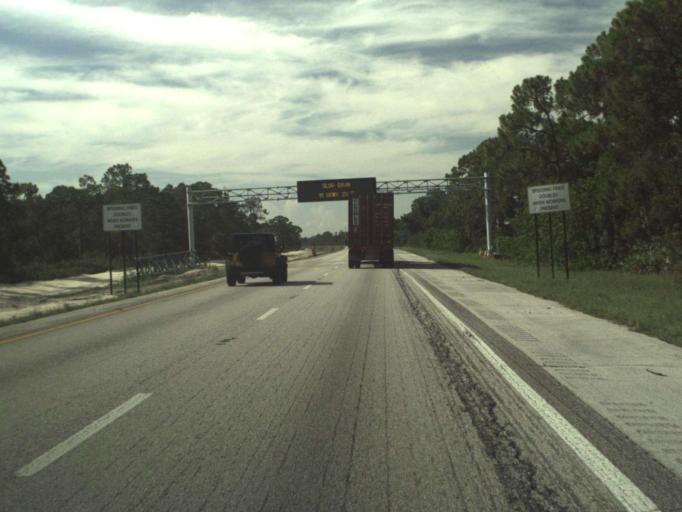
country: US
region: Florida
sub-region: Indian River County
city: West Vero Corridor
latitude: 27.6649
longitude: -80.5290
